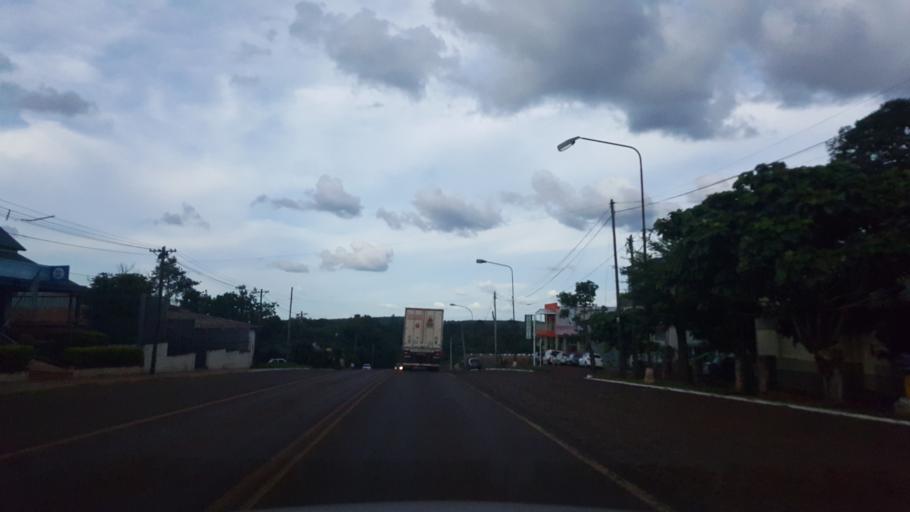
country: AR
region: Misiones
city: Gobernador Roca
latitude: -27.1852
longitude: -55.4633
